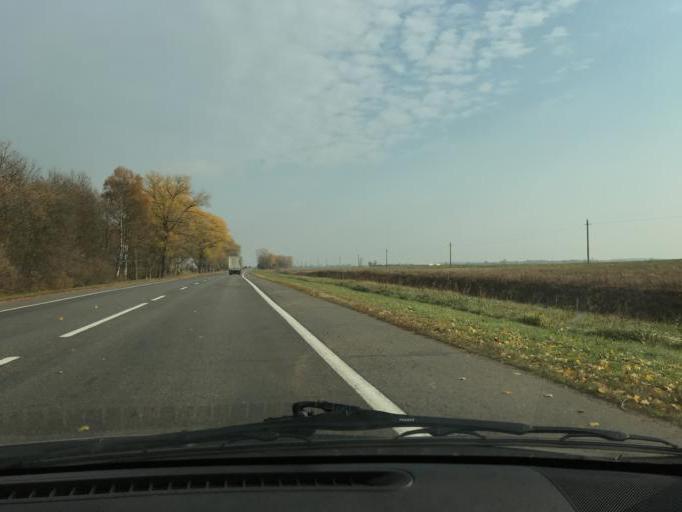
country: BY
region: Vitebsk
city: Chashniki
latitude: 55.0088
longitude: 28.9807
